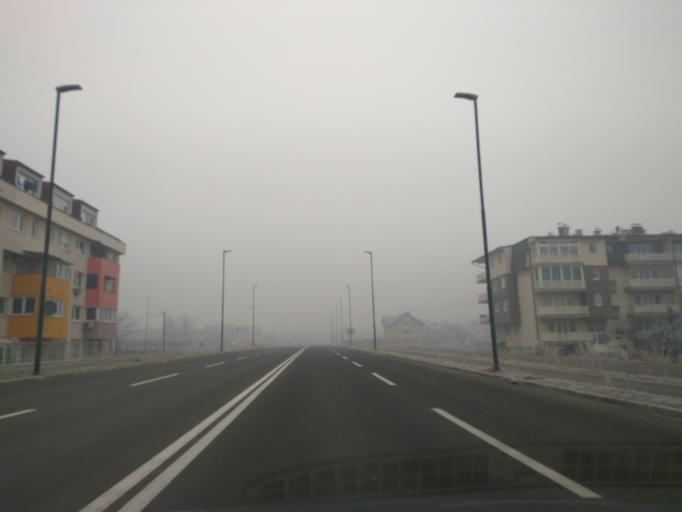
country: BA
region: Federation of Bosnia and Herzegovina
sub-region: Kanton Sarajevo
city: Sarajevo
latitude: 43.8325
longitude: 18.3369
